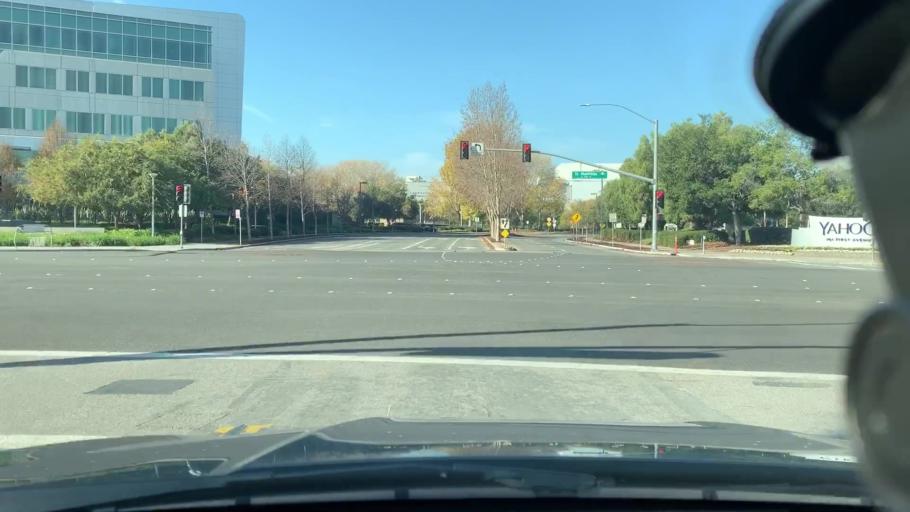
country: US
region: California
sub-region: Santa Clara County
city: Sunnyvale
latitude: 37.4161
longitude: -122.0244
